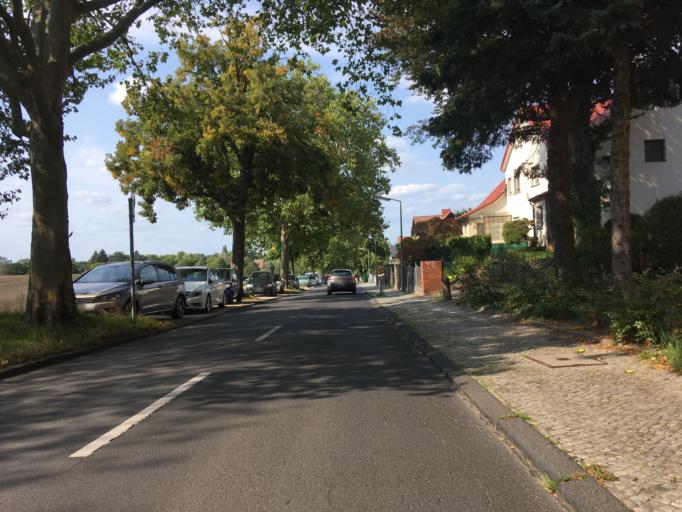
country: DE
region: Berlin
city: Lubars
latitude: 52.6139
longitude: 13.3434
